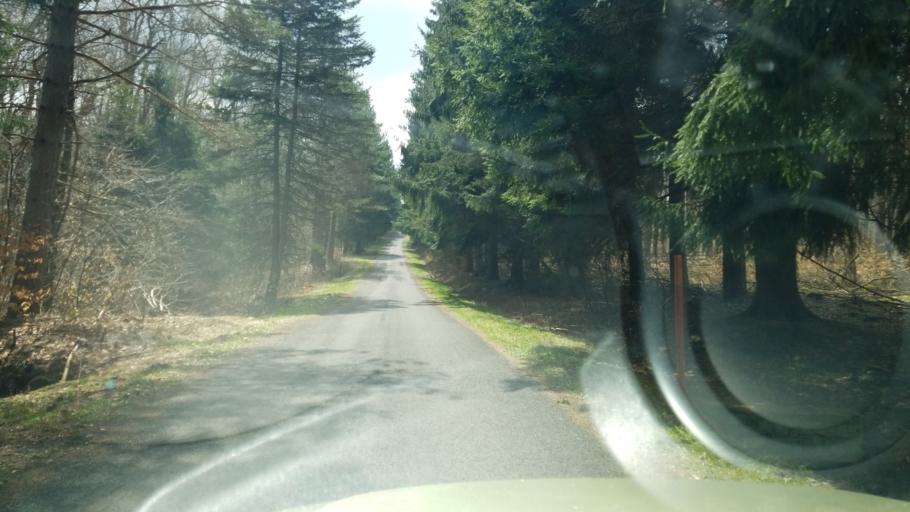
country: US
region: Pennsylvania
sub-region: Jefferson County
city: Brockway
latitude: 41.2829
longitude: -78.8717
